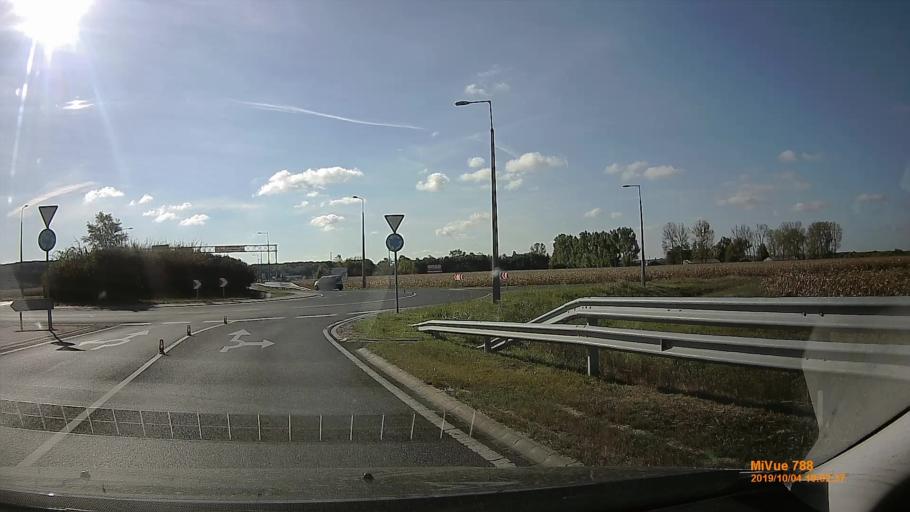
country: HU
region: Somogy
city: Kaposvar
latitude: 46.3962
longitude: 17.7769
